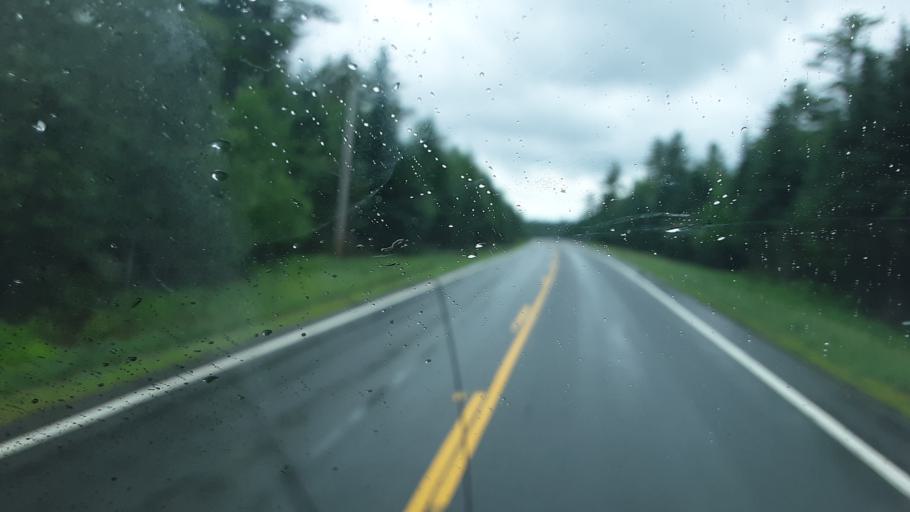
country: US
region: Maine
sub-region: Penobscot County
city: Patten
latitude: 46.4051
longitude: -68.3633
